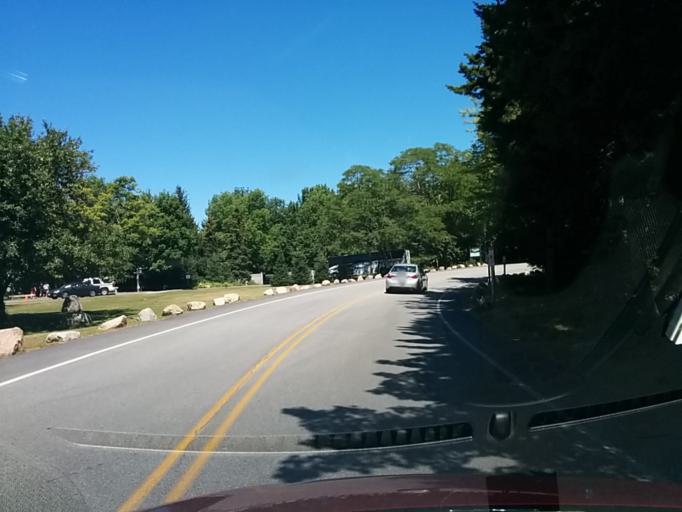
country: US
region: Maine
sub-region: Hancock County
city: Bar Harbor
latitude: 44.3198
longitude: -68.2528
